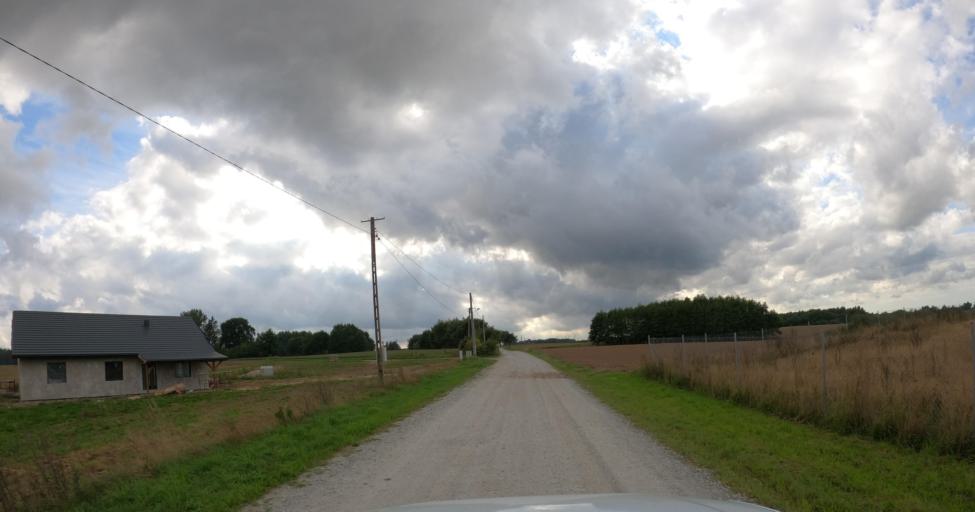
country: PL
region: West Pomeranian Voivodeship
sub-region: Powiat kolobrzeski
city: Goscino
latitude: 54.0735
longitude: 15.5992
